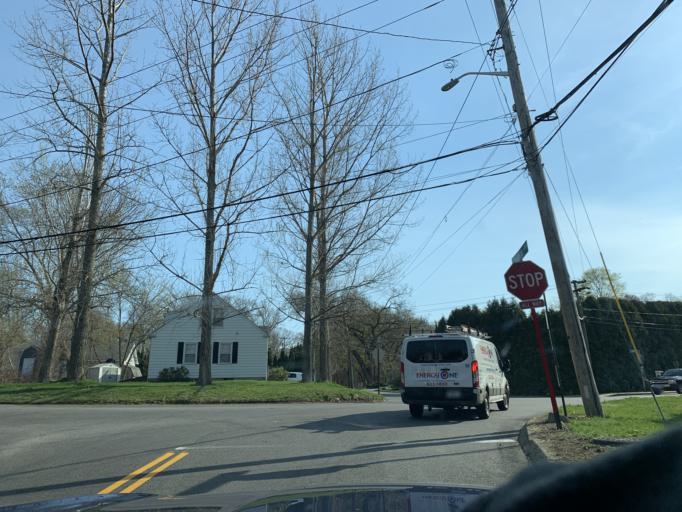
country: US
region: Rhode Island
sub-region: Kent County
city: West Warwick
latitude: 41.7537
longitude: -71.4984
